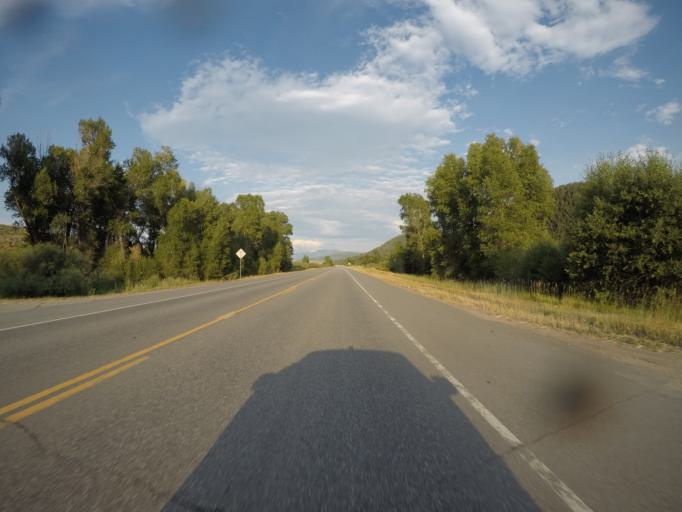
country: US
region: Colorado
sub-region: Routt County
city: Steamboat Springs
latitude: 40.4862
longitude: -106.9945
